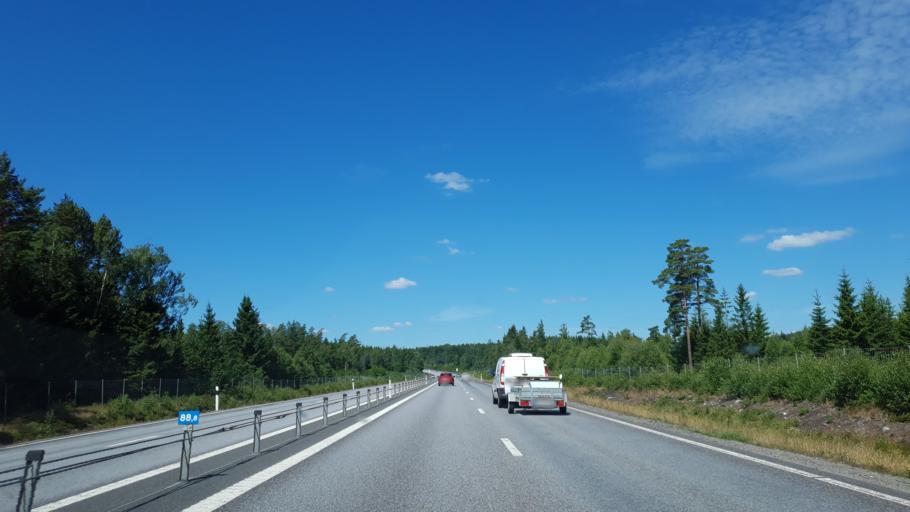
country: SE
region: Kronoberg
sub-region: Vaxjo Kommun
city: Gemla
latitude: 56.9162
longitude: 14.6207
